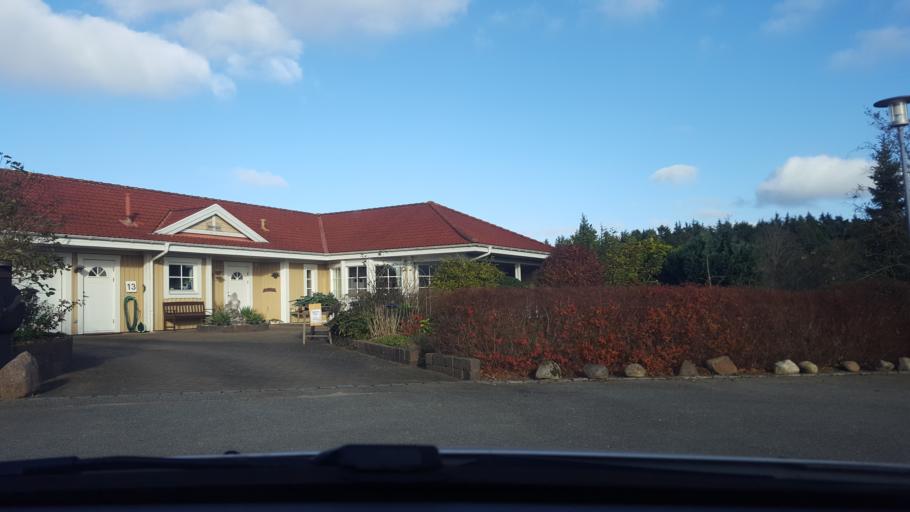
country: DK
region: North Denmark
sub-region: Morso Kommune
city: Nykobing Mors
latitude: 56.7475
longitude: 8.8683
